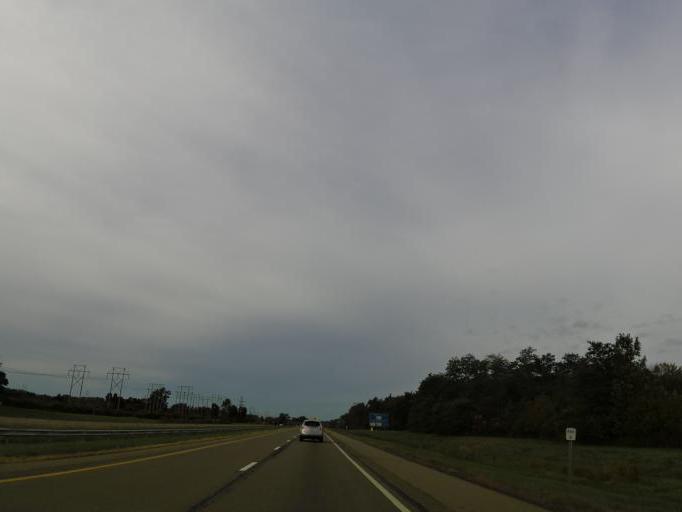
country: US
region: New York
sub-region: Chautauqua County
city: Dunkirk
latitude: 42.4694
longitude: -79.2857
